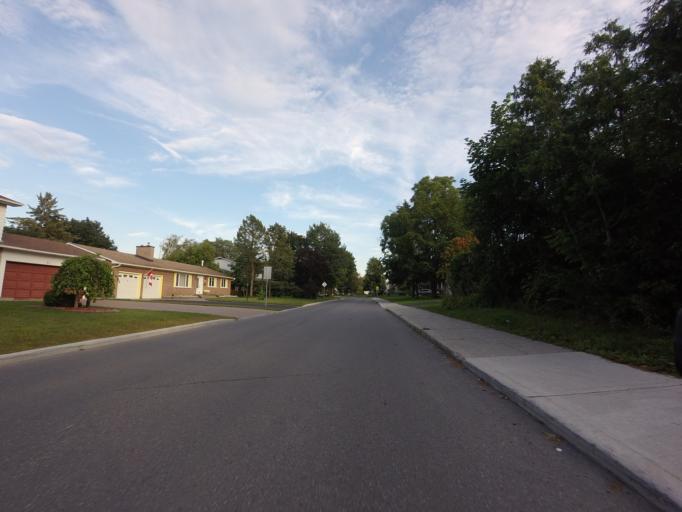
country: CA
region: Ontario
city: Bells Corners
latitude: 45.2822
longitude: -75.7658
